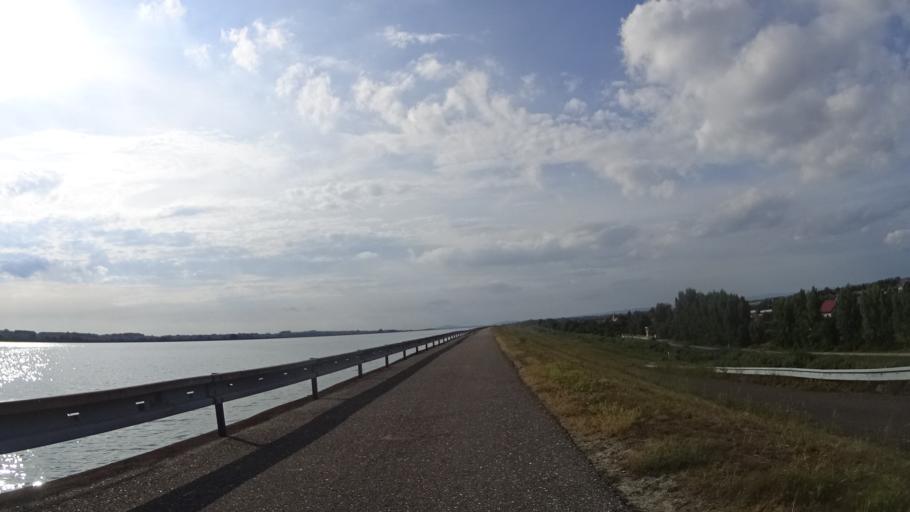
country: HU
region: Gyor-Moson-Sopron
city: Asvanyraro
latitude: 47.9455
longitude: 17.4462
